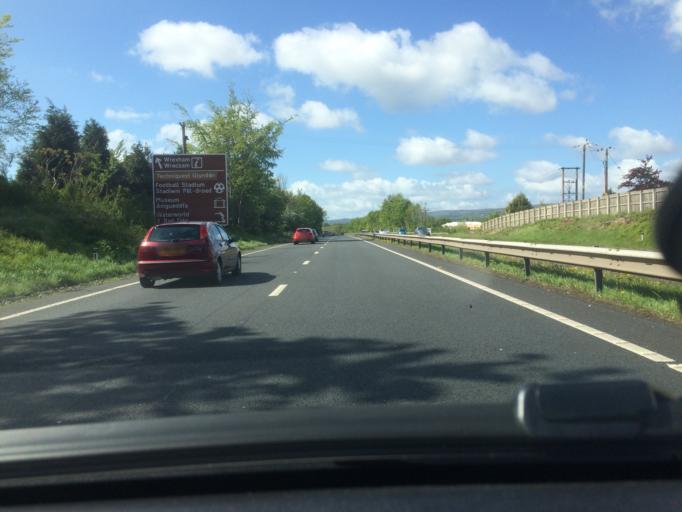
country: GB
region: Wales
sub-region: Wrexham
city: Wrexham
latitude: 53.0639
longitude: -3.0011
